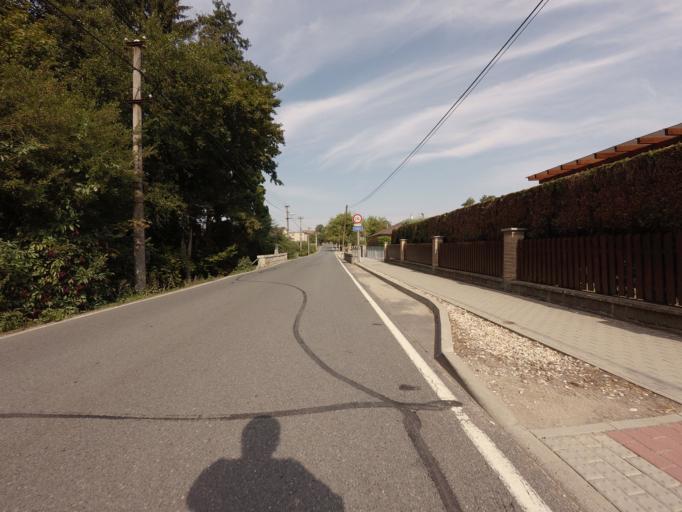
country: CZ
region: Central Bohemia
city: Petrovice
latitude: 49.5513
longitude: 14.3422
